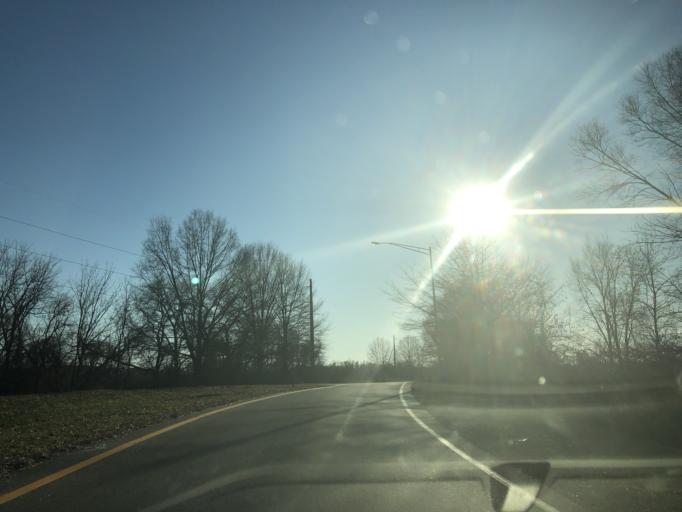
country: US
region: New Jersey
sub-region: Salem County
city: Carneys Point
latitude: 39.7101
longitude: -75.4486
